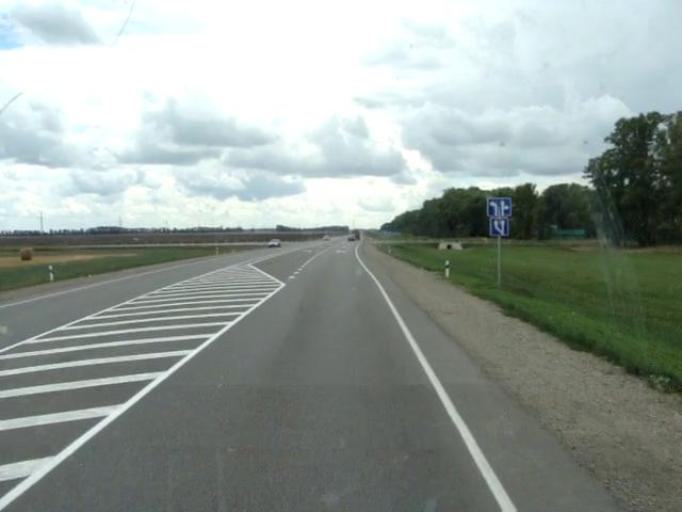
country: RU
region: Altai Krai
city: Shubenka
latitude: 52.6775
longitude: 85.0504
